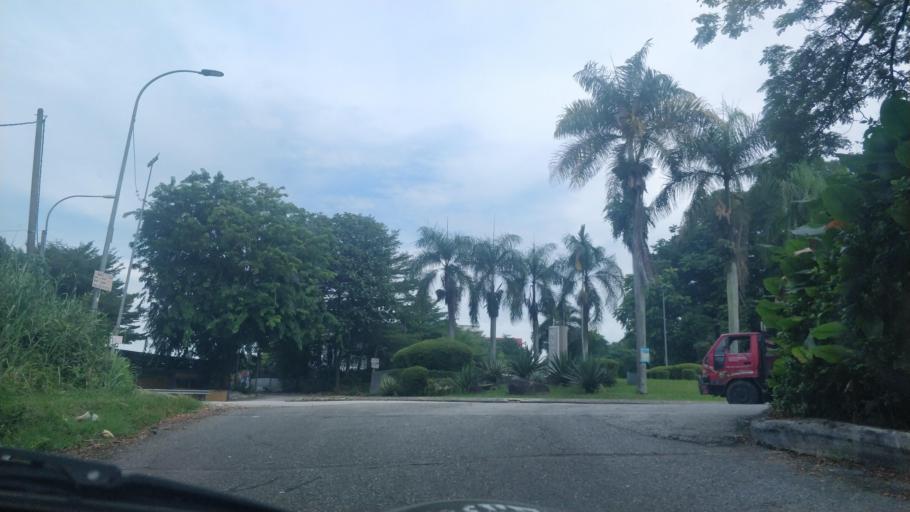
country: MY
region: Selangor
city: Kuang
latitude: 3.2024
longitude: 101.5901
